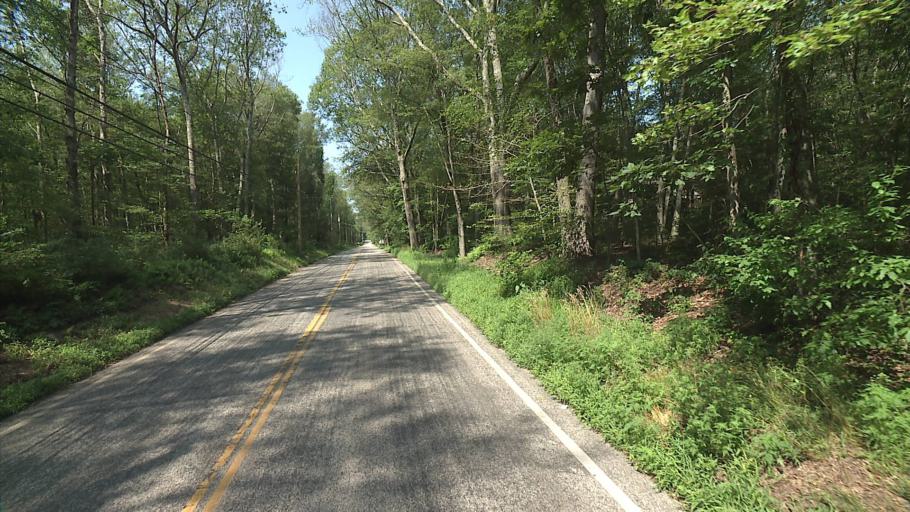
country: US
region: Connecticut
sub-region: New London County
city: Colchester
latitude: 41.5754
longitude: -72.2904
